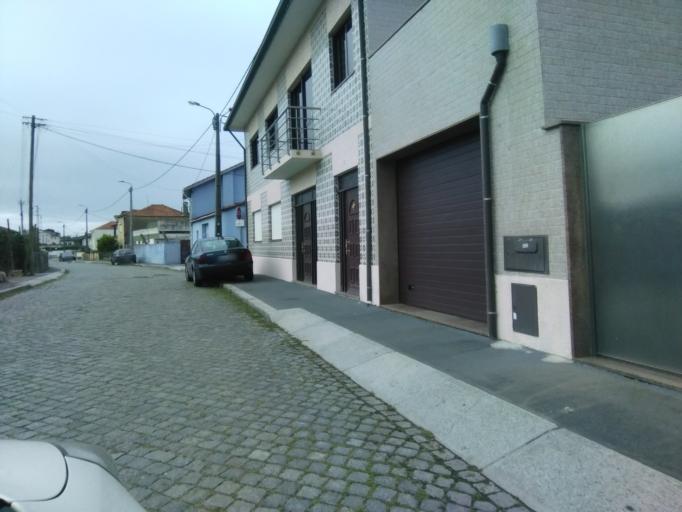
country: PT
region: Porto
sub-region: Matosinhos
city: Lavra
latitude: 41.2365
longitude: -8.7174
